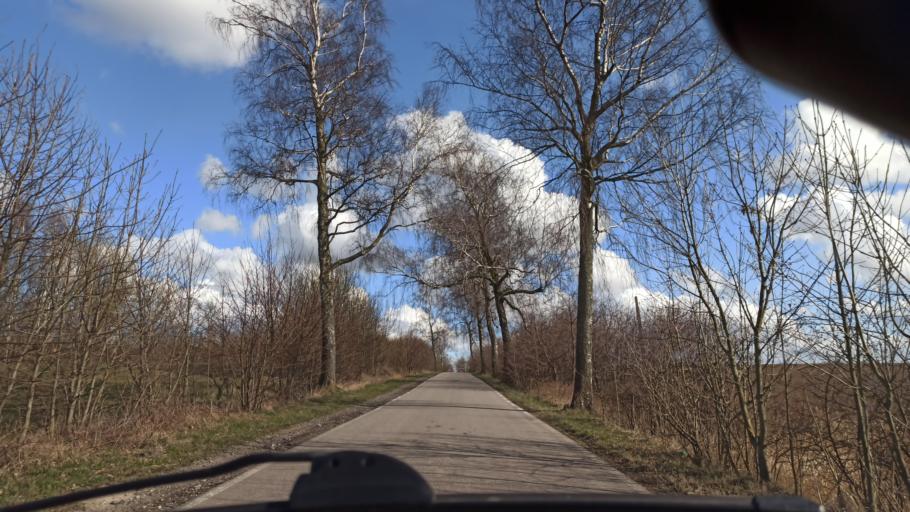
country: PL
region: Warmian-Masurian Voivodeship
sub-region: Powiat elblaski
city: Tolkmicko
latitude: 54.2654
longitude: 19.4819
